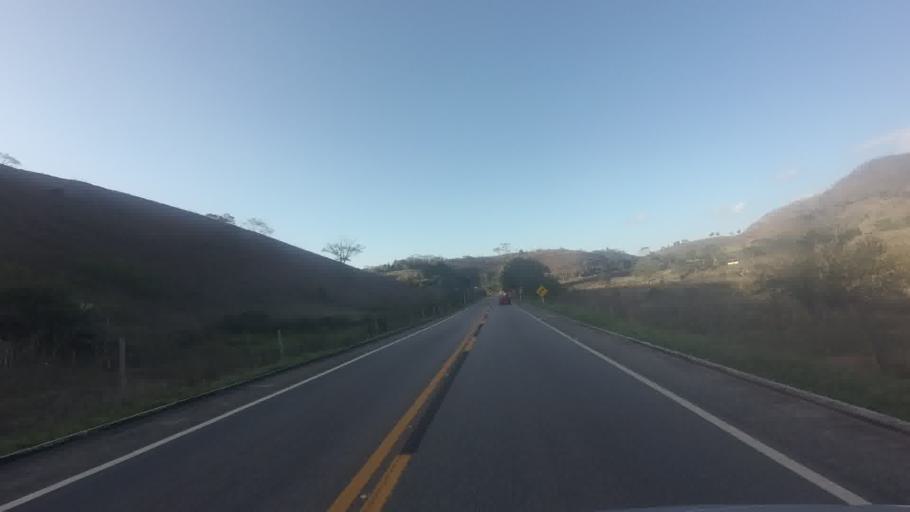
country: BR
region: Espirito Santo
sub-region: Jeronimo Monteiro
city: Jeronimo Monteiro
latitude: -20.8815
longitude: -41.2691
